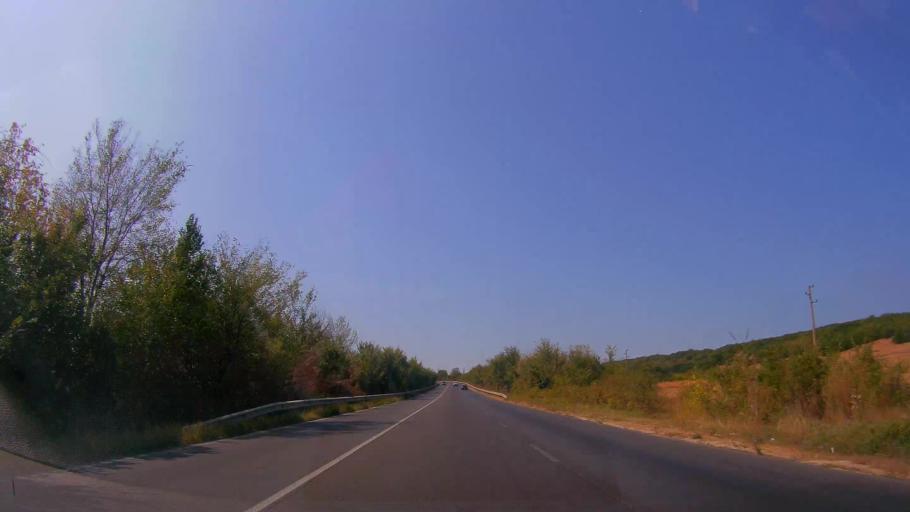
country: BG
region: Ruse
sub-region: Obshtina Vetovo
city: Senovo
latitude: 43.5610
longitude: 26.3825
